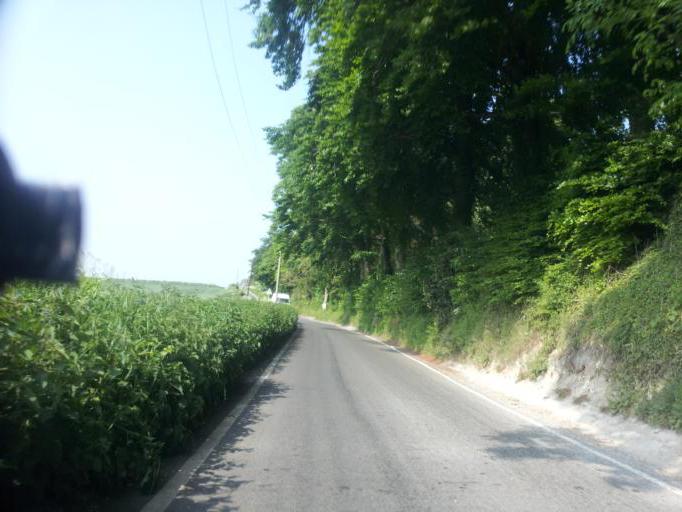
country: GB
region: England
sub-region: Medway
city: Cuxton
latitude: 51.3558
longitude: 0.4729
